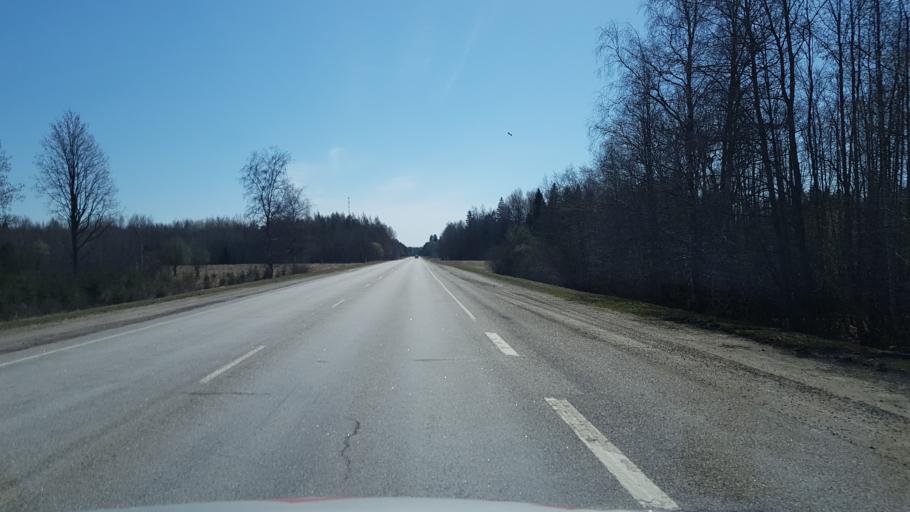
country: EE
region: Ida-Virumaa
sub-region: Johvi vald
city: Johvi
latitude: 59.1739
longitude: 27.3503
